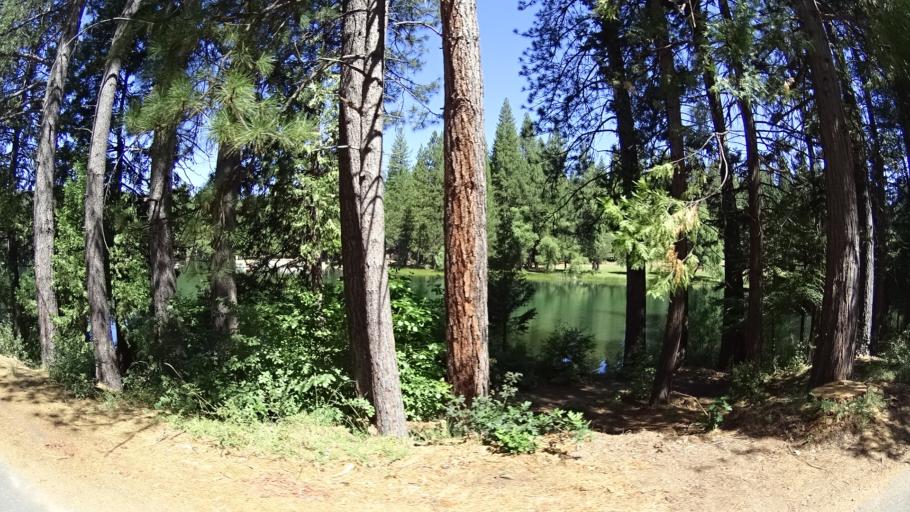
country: US
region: California
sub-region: Calaveras County
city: Arnold
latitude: 38.2339
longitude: -120.3725
